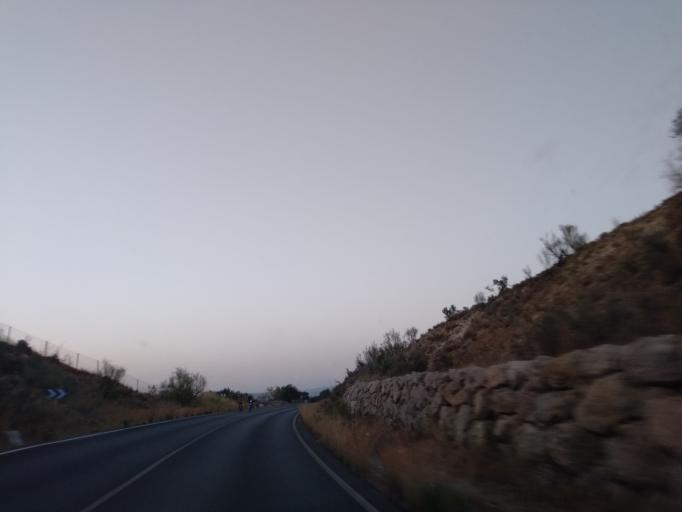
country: ES
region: Andalusia
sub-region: Provincia de Malaga
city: Cartama
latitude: 36.6950
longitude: -4.6512
